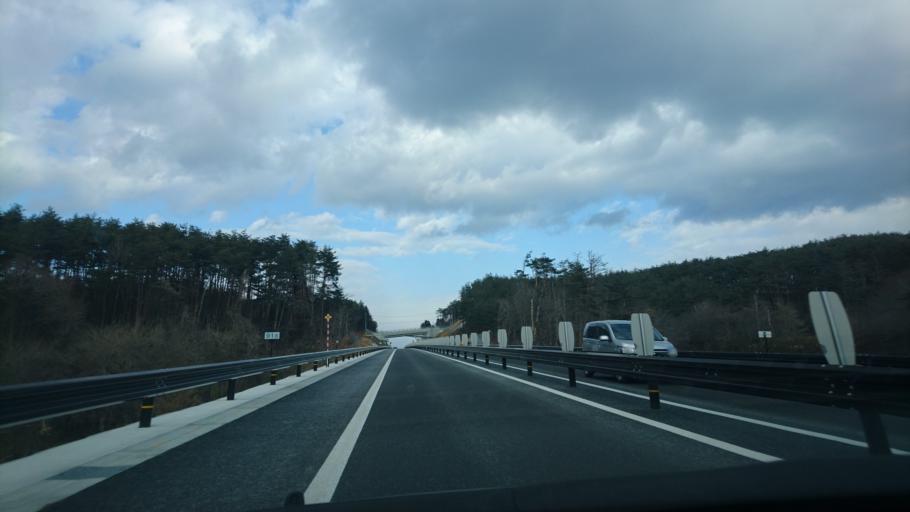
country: JP
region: Miyagi
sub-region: Oshika Gun
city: Onagawa Cho
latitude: 38.7276
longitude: 141.5156
